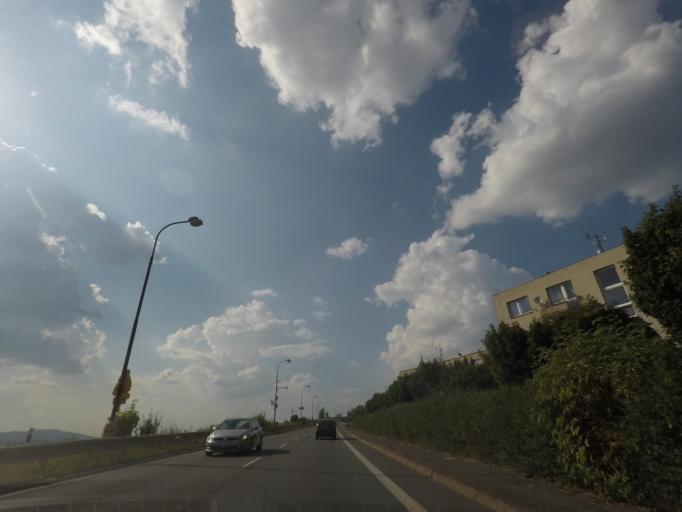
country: CZ
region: Kralovehradecky
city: Dvur Kralove nad Labem
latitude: 50.4250
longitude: 15.8755
